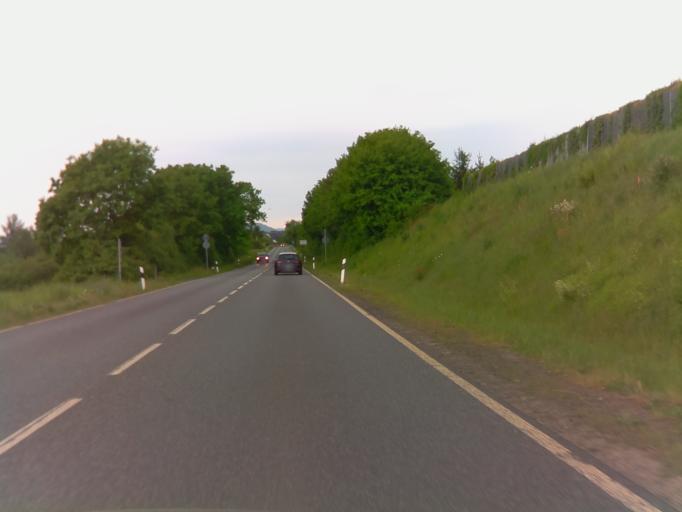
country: DE
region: Hesse
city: Stadtallendorf
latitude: 50.8340
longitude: 9.0252
